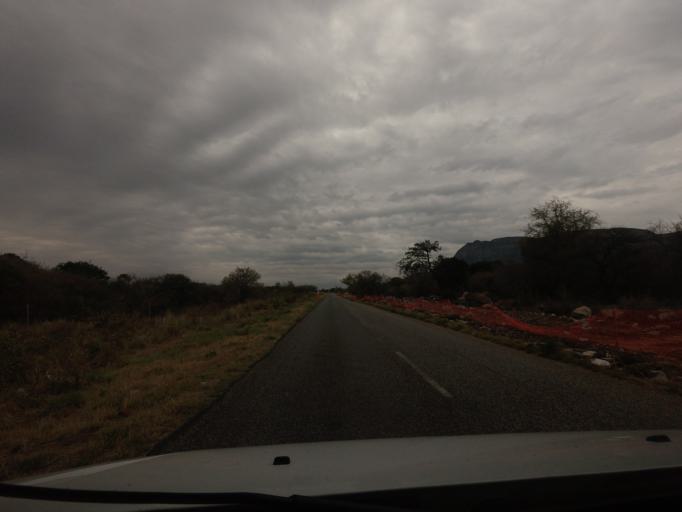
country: ZA
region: Limpopo
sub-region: Mopani District Municipality
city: Hoedspruit
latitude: -24.5038
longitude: 30.8994
